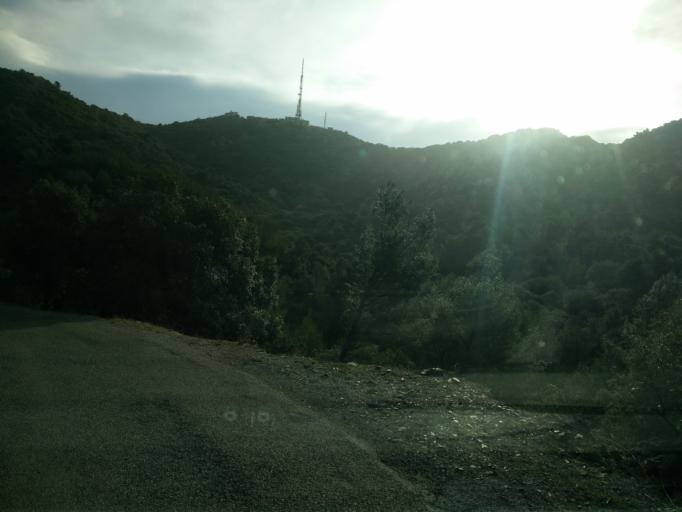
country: FR
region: Provence-Alpes-Cote d'Azur
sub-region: Departement du Var
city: Six-Fours-les-Plages
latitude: 43.0575
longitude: 5.8389
